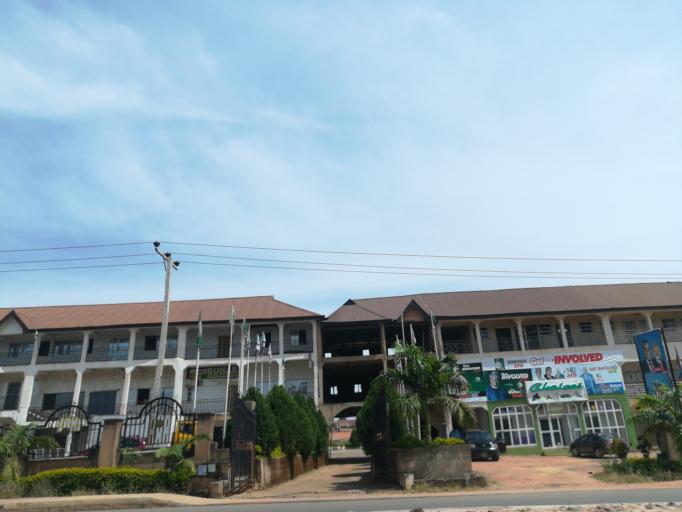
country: NG
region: Plateau
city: Bukuru
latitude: 9.8477
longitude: 8.8670
